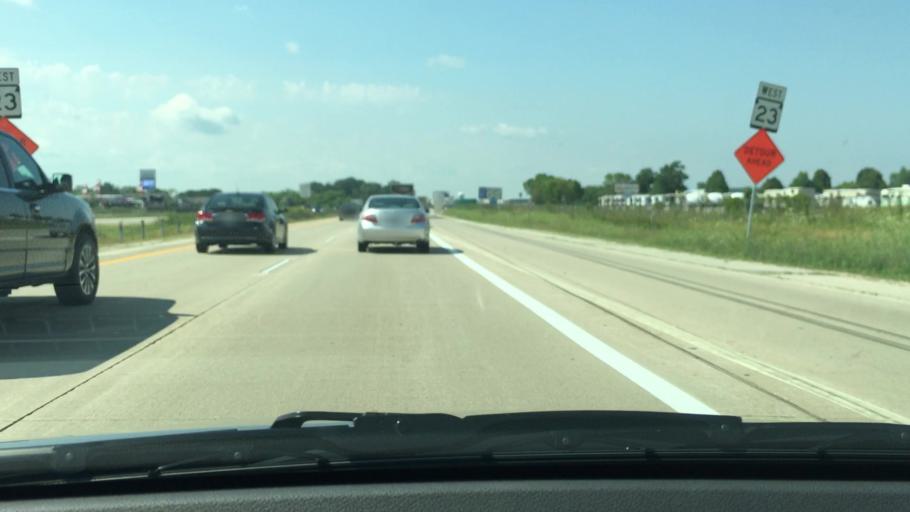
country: US
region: Wisconsin
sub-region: Fond du Lac County
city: Fond du Lac
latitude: 43.7627
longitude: -88.4782
